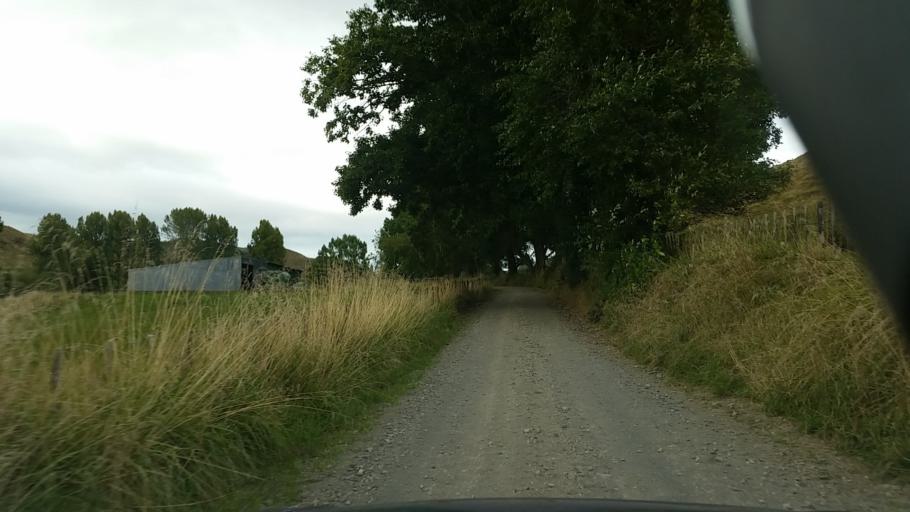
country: NZ
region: Taranaki
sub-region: South Taranaki District
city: Eltham
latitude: -39.3477
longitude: 174.5124
